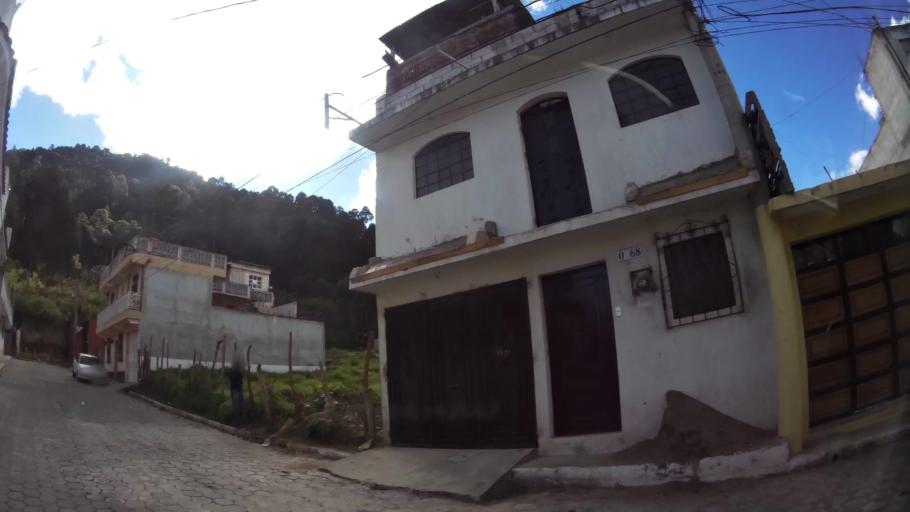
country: GT
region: Quetzaltenango
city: Quetzaltenango
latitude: 14.8321
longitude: -91.5081
